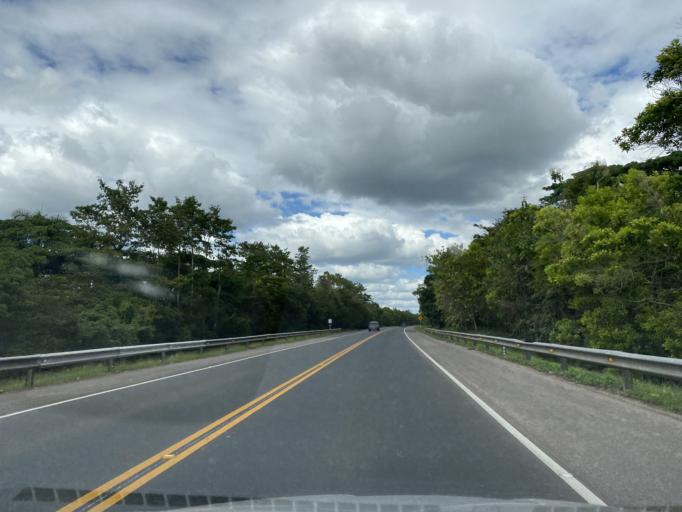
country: DO
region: Santo Domingo
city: Guerra
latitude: 18.6021
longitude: -69.7709
